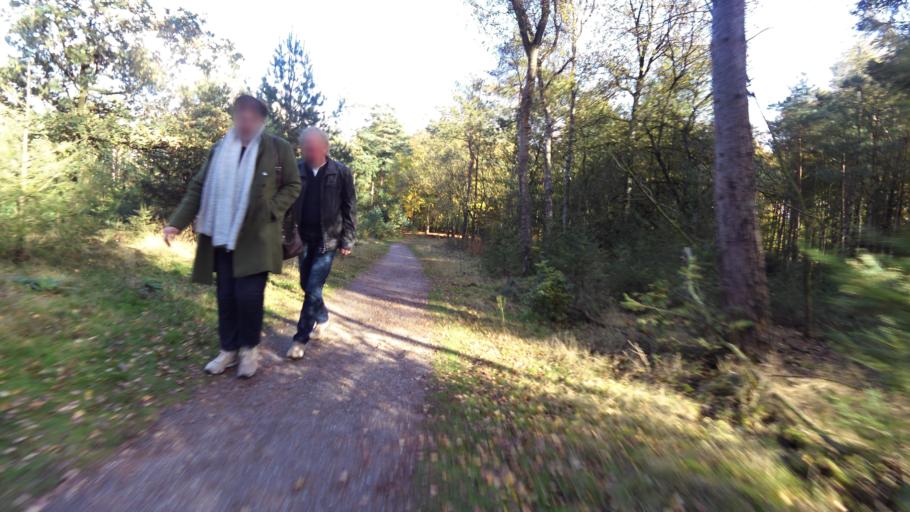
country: NL
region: Gelderland
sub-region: Gemeente Epe
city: Epe
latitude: 52.3827
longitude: 5.9533
